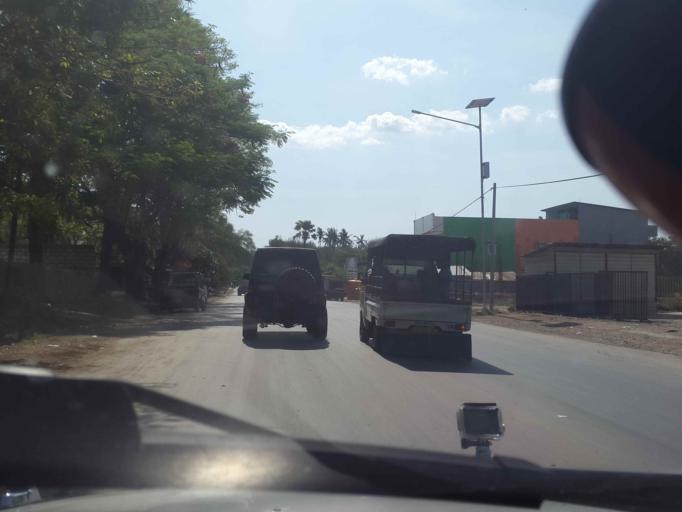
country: ID
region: East Nusa Tenggara
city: Oesapa
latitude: -10.1495
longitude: 123.6415
